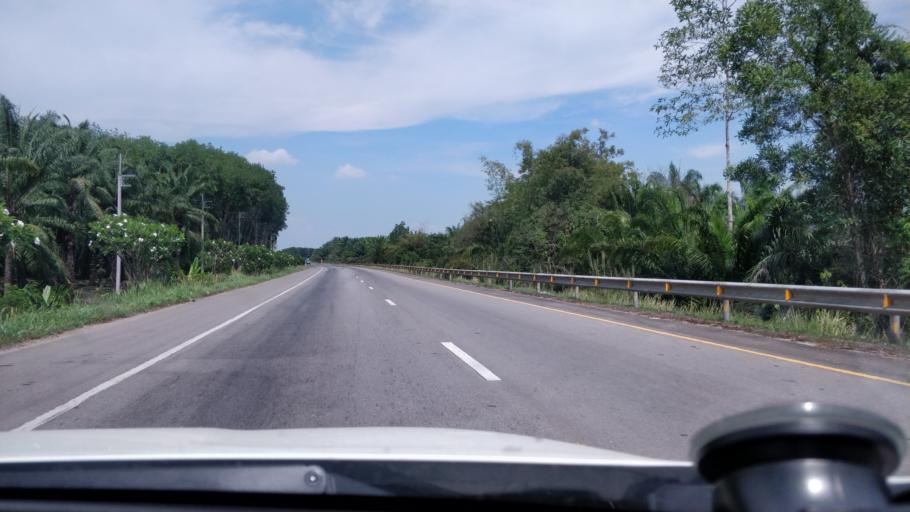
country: TH
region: Surat Thani
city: Chai Buri
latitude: 8.6413
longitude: 99.0781
